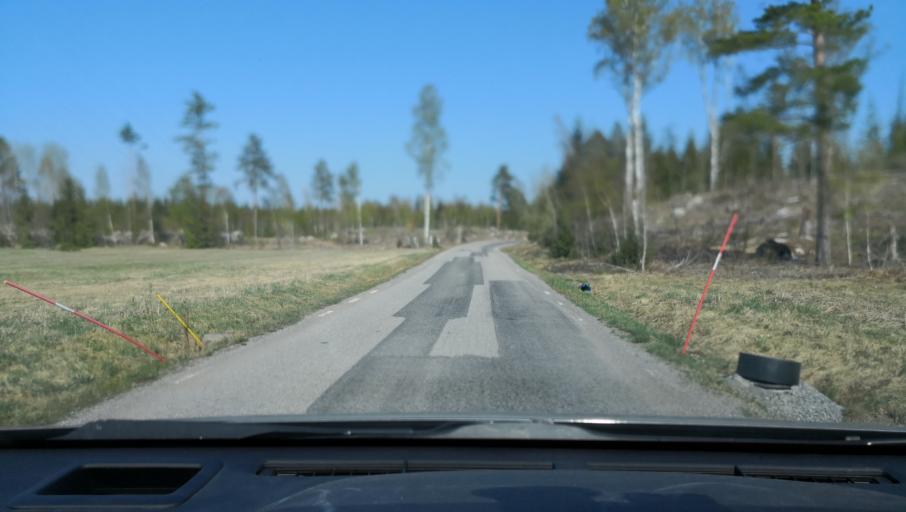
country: SE
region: Uppsala
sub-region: Heby Kommun
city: Heby
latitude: 60.0353
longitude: 16.8133
